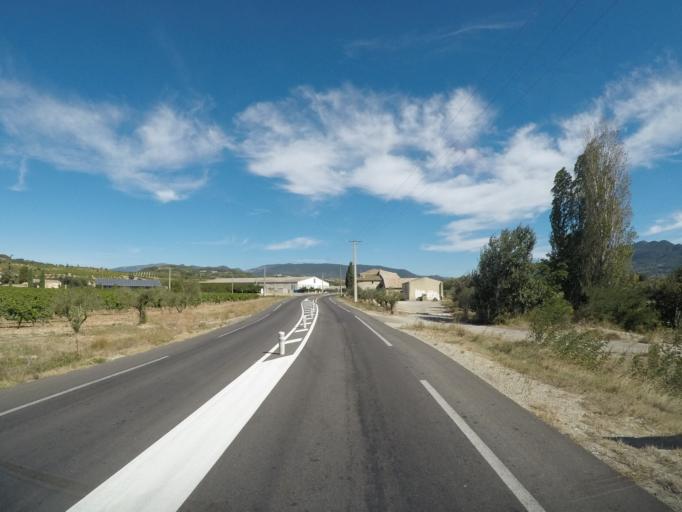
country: FR
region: Rhone-Alpes
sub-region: Departement de la Drome
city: Vinsobres
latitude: 44.3227
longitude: 5.0715
